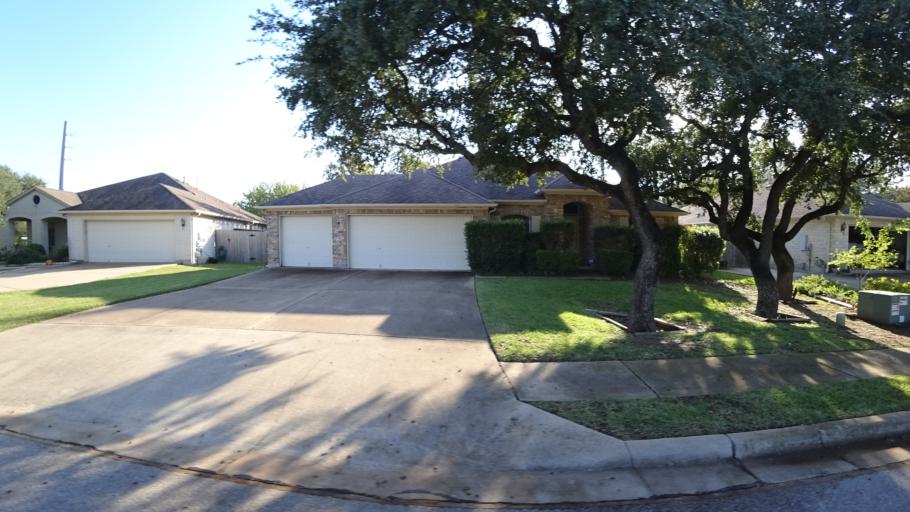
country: US
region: Texas
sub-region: Travis County
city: Shady Hollow
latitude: 30.2181
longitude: -97.8515
